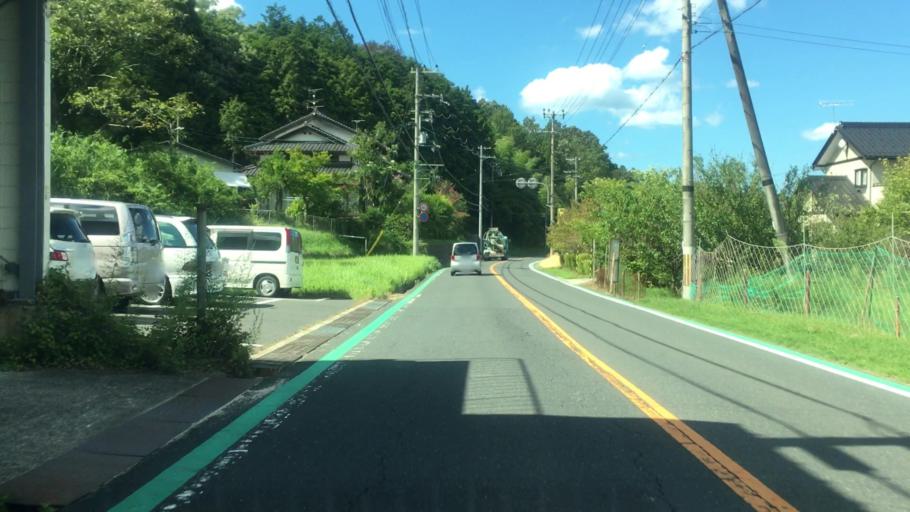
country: JP
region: Kyoto
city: Miyazu
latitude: 35.6162
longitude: 135.0536
